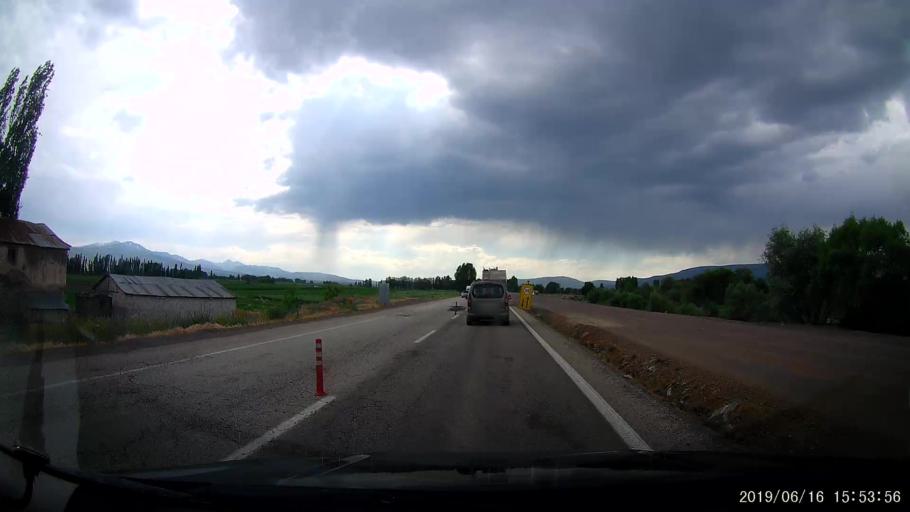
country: TR
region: Erzurum
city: Pasinler
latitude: 39.9775
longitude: 41.6406
